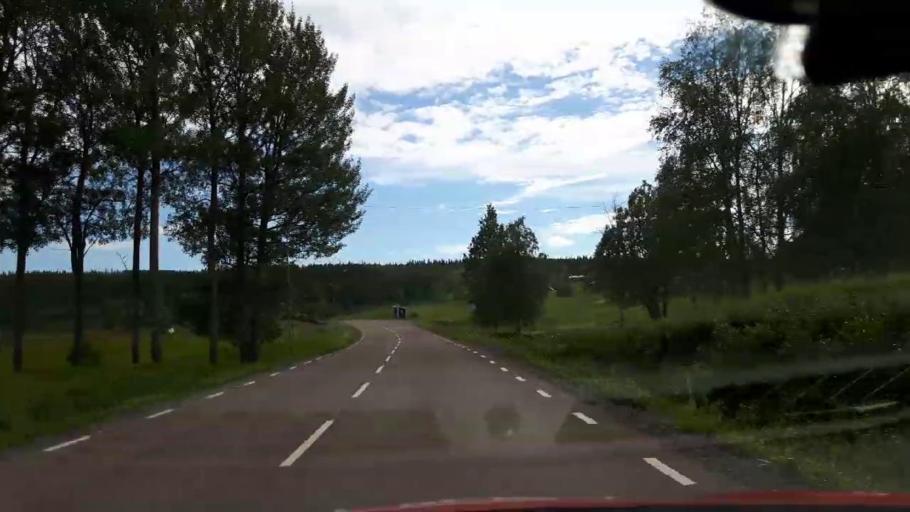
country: SE
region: Jaemtland
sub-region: Krokoms Kommun
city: Valla
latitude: 63.9080
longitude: 14.2140
